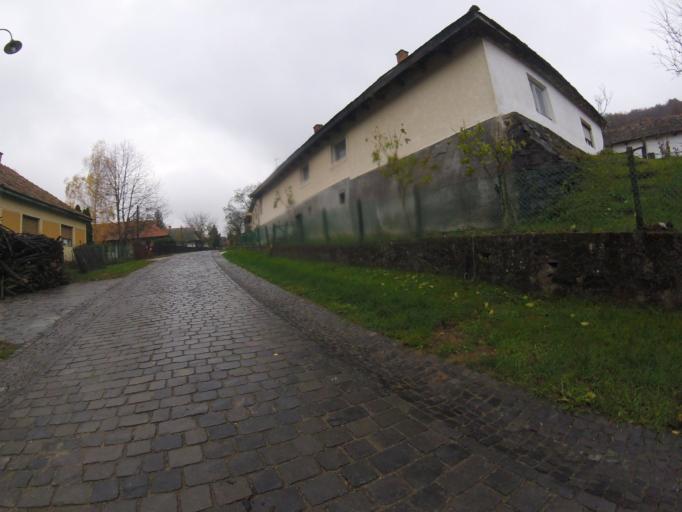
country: HU
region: Nograd
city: Rimoc
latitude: 47.9997
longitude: 19.5839
